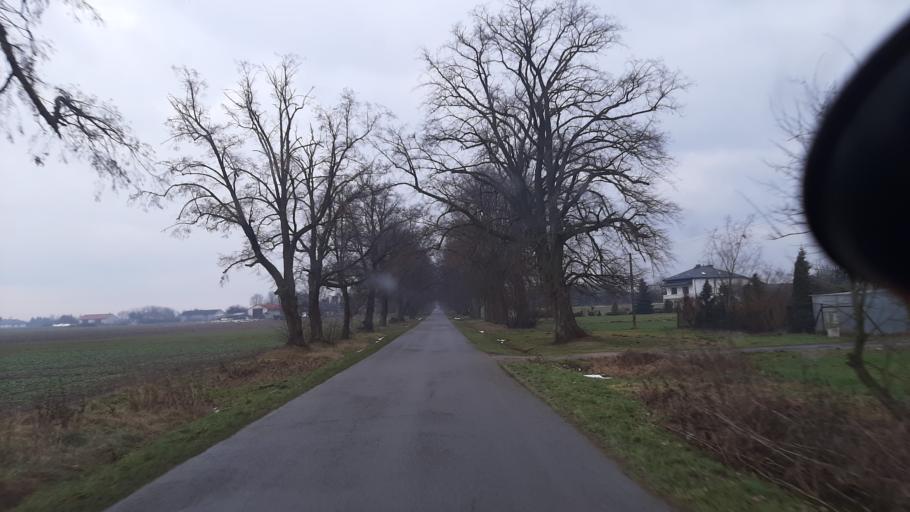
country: PL
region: Lublin Voivodeship
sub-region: Powiat lubelski
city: Lublin
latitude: 51.3428
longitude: 22.5307
